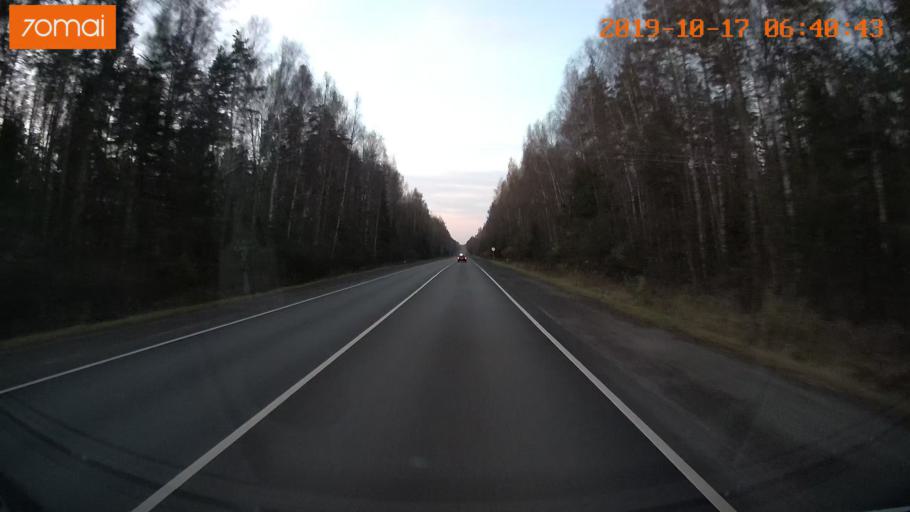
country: RU
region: Ivanovo
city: Nerl'
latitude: 56.6252
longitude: 40.5670
